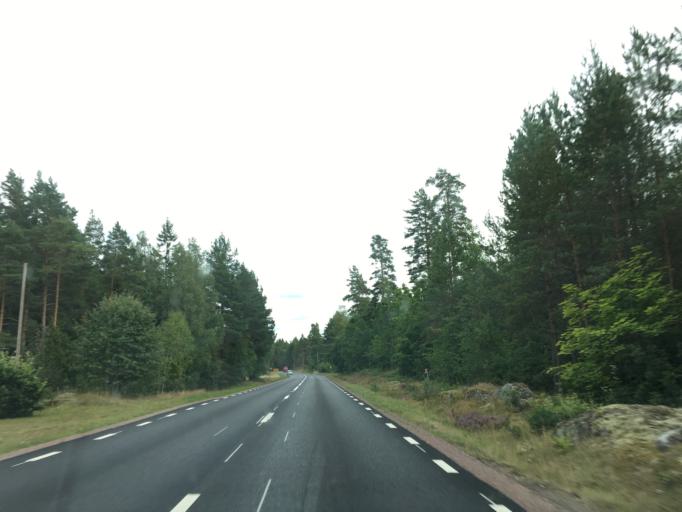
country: SE
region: Kalmar
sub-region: Nybro Kommun
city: Nybro
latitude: 56.9231
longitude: 15.9503
